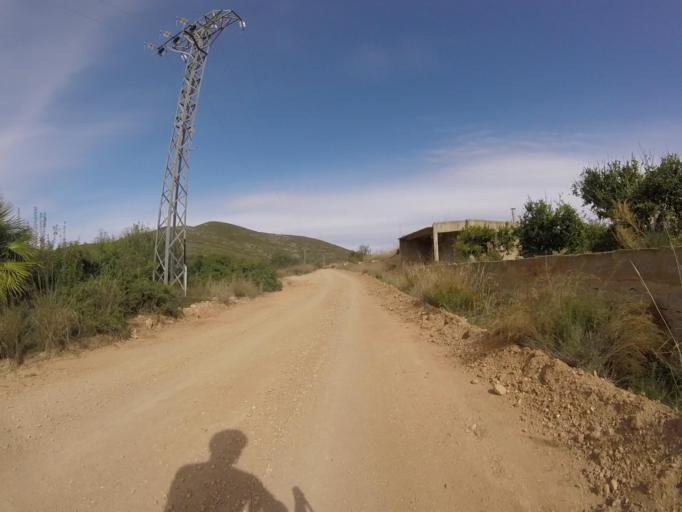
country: ES
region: Valencia
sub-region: Provincia de Castello
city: Torreblanca
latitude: 40.1960
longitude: 0.1594
